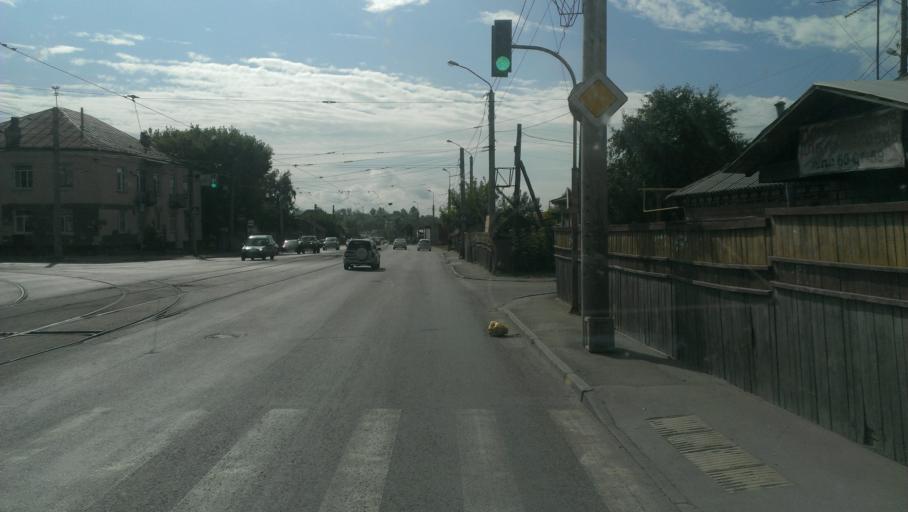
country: RU
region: Altai Krai
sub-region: Gorod Barnaulskiy
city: Barnaul
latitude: 53.3446
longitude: 83.7339
